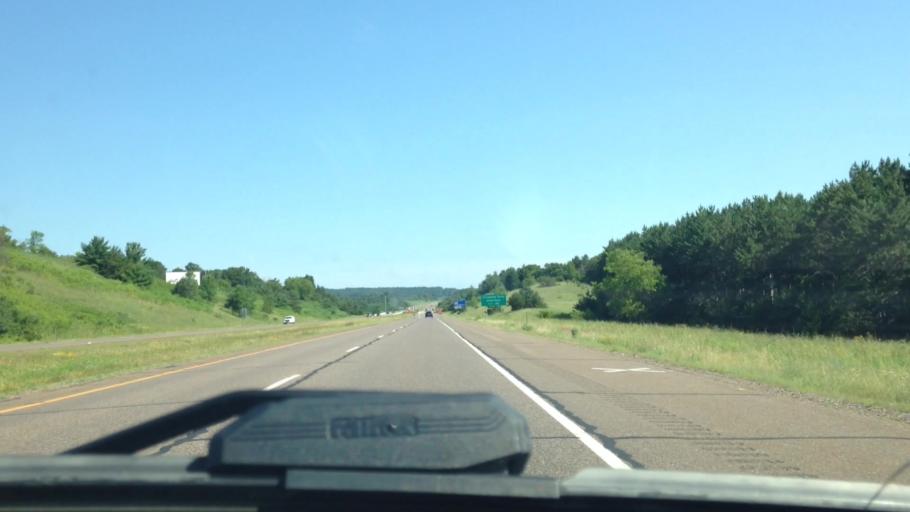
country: US
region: Wisconsin
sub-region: Chippewa County
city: Chippewa Falls
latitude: 44.9156
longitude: -91.4278
